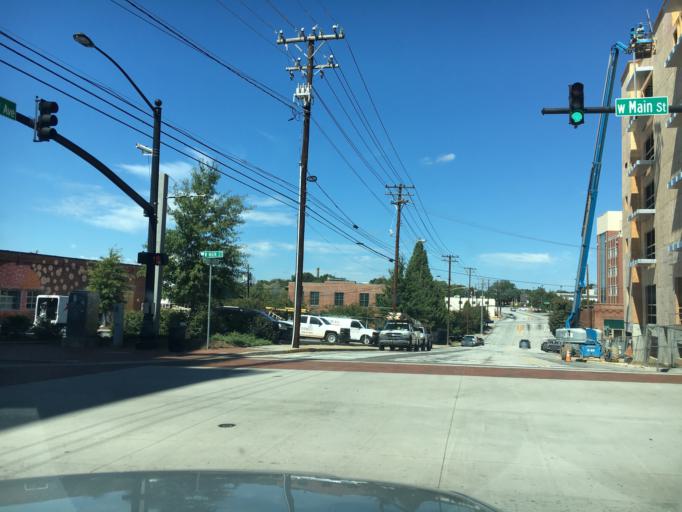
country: US
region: South Carolina
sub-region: Spartanburg County
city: Spartanburg
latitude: 34.9485
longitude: -81.9349
